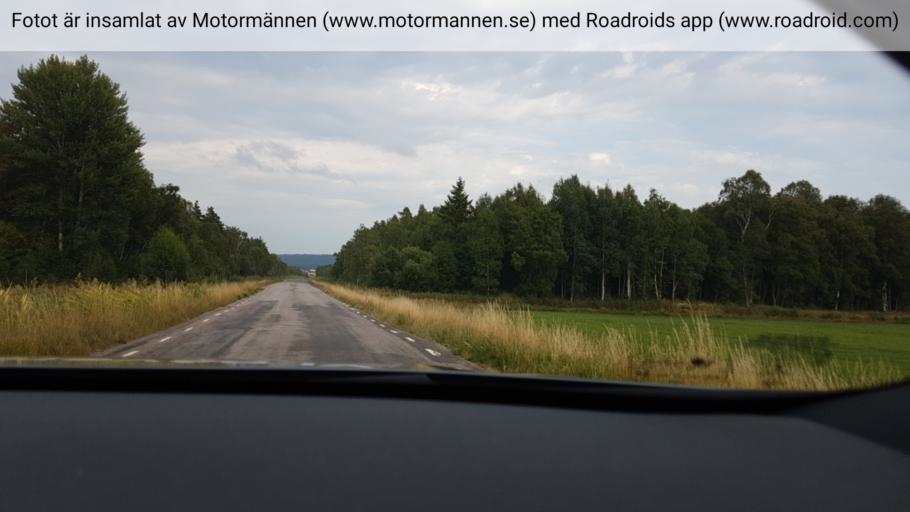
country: SE
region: Vaestra Goetaland
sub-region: Falkopings Kommun
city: Akarp
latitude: 58.1776
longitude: 13.6514
